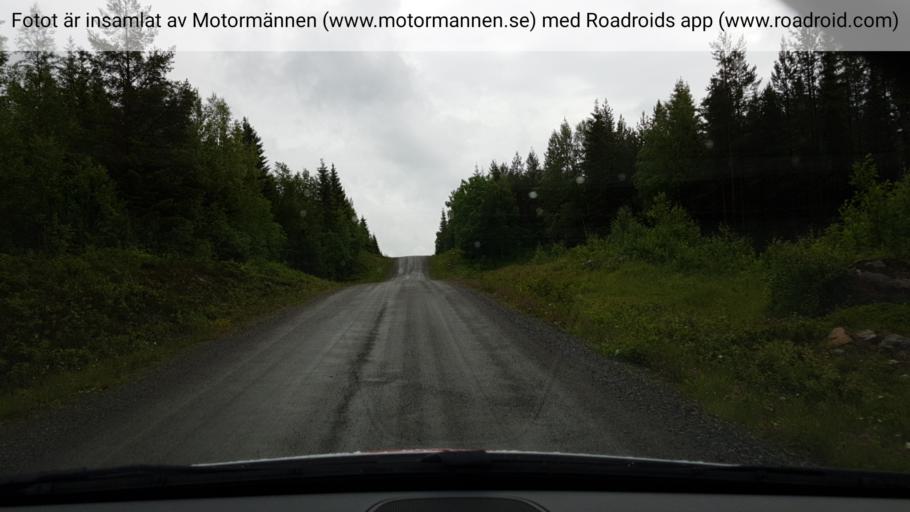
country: SE
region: Jaemtland
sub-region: Stroemsunds Kommun
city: Stroemsund
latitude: 64.2558
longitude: 15.0242
